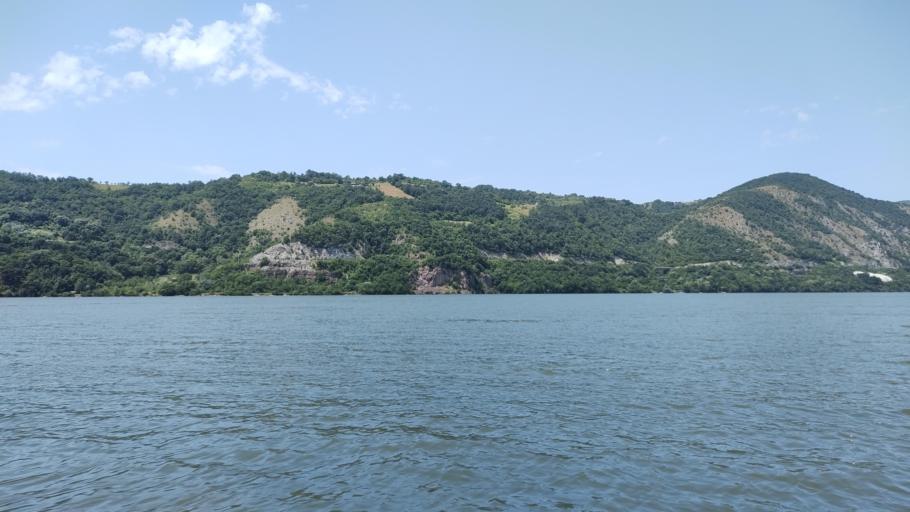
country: RO
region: Mehedinti
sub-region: Comuna Svinita
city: Svinita
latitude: 44.5462
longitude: 22.0400
